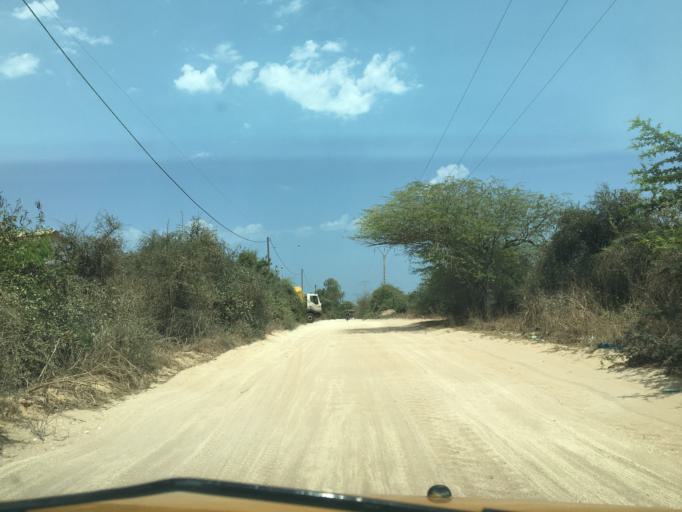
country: SN
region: Thies
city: Thies
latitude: 14.8227
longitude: -17.2034
